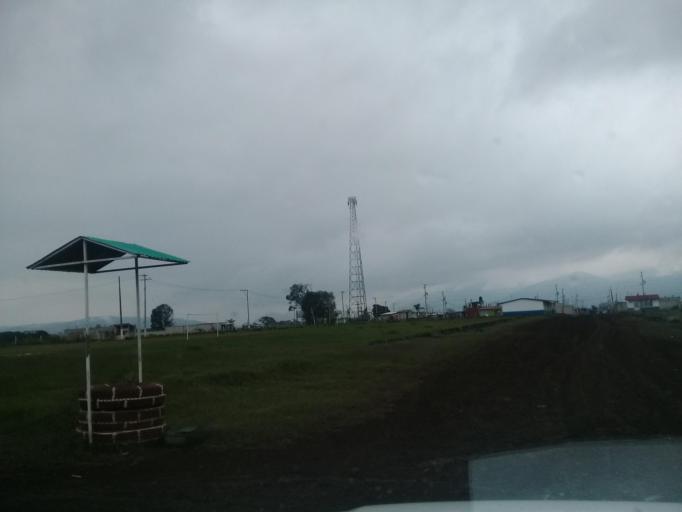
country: MX
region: Veracruz
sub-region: Cordoba
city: San Jose de Tapia
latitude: 18.8547
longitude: -96.9595
